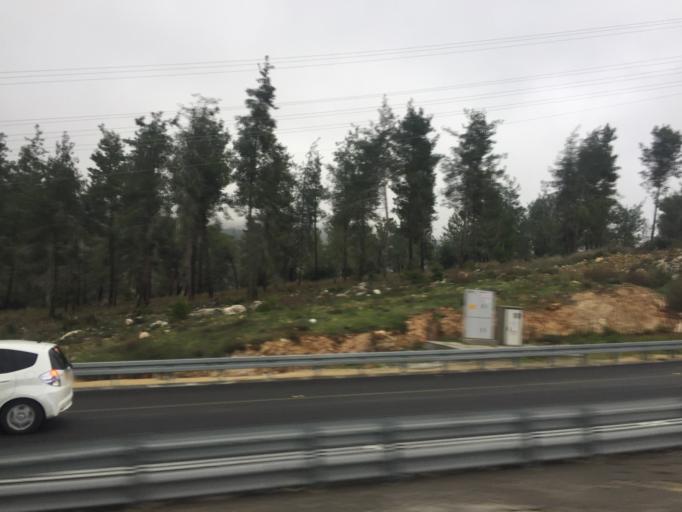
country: IL
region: Jerusalem
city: Abu Ghaush
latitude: 31.8005
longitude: 35.1347
